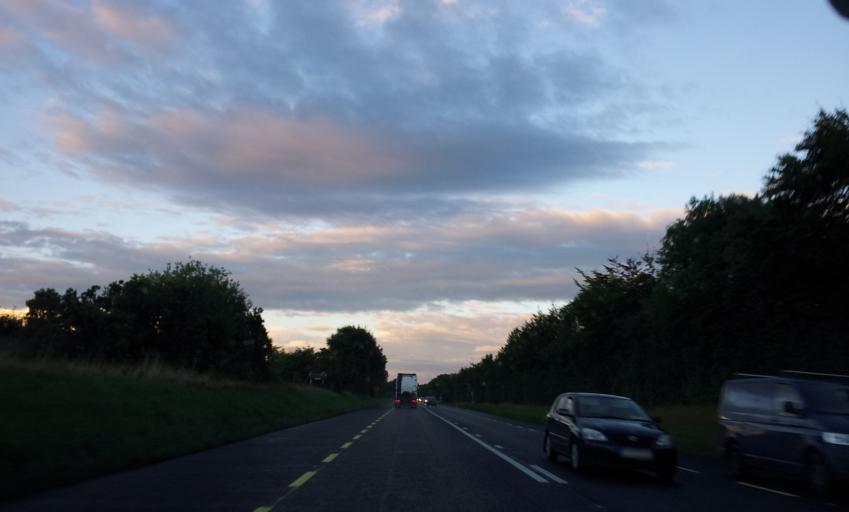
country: IE
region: Munster
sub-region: County Limerick
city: Adare
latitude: 52.5450
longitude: -8.8435
